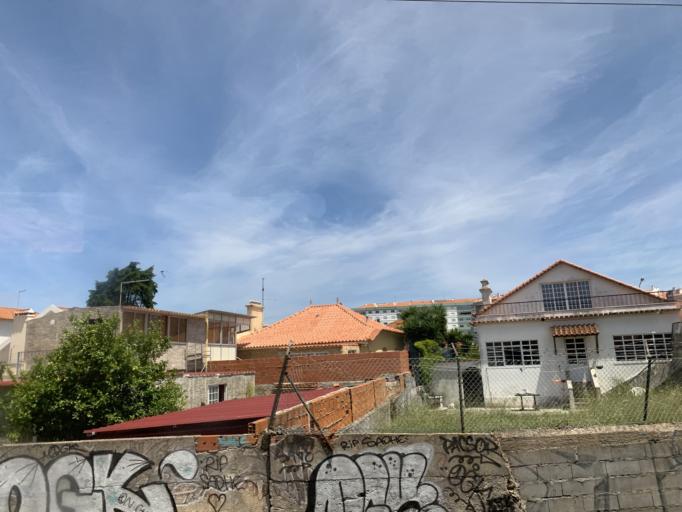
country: PT
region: Lisbon
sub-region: Sintra
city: Rio de Mouro
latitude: 38.7980
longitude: -9.3384
